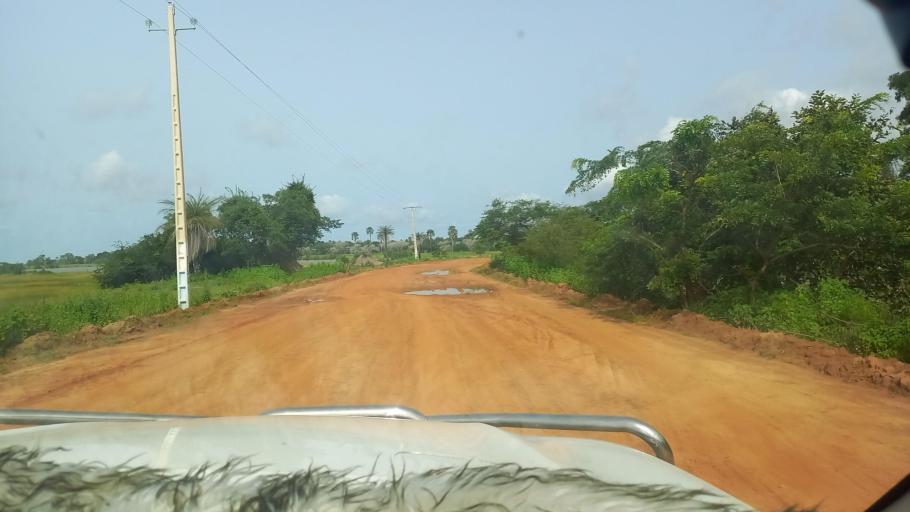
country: SN
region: Ziguinchor
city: Ziguinchor
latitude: 12.6712
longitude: -16.2783
